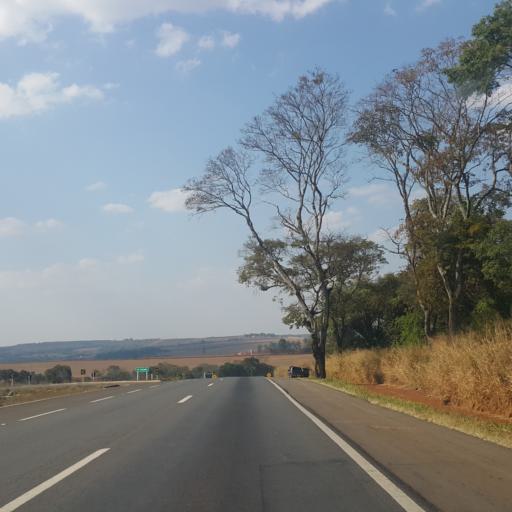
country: BR
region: Goias
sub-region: Abadiania
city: Abadiania
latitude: -16.2815
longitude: -48.7922
